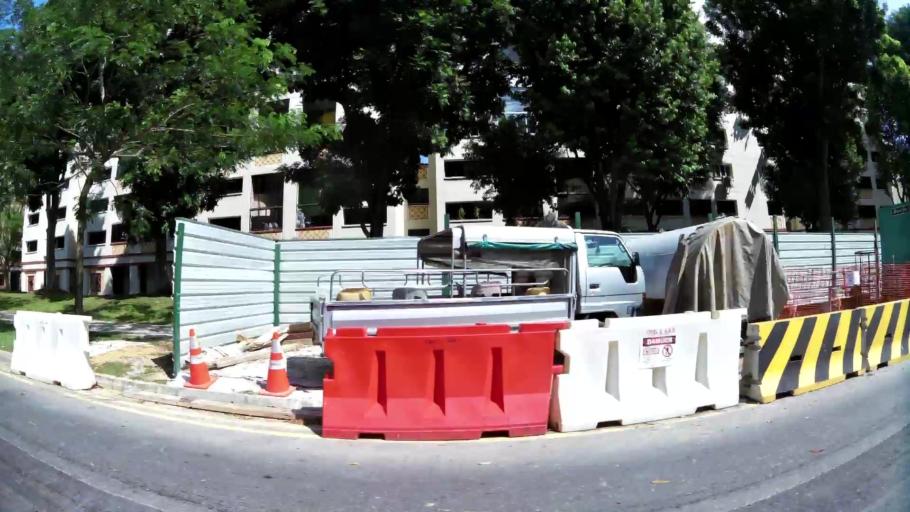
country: SG
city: Singapore
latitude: 1.3771
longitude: 103.8389
